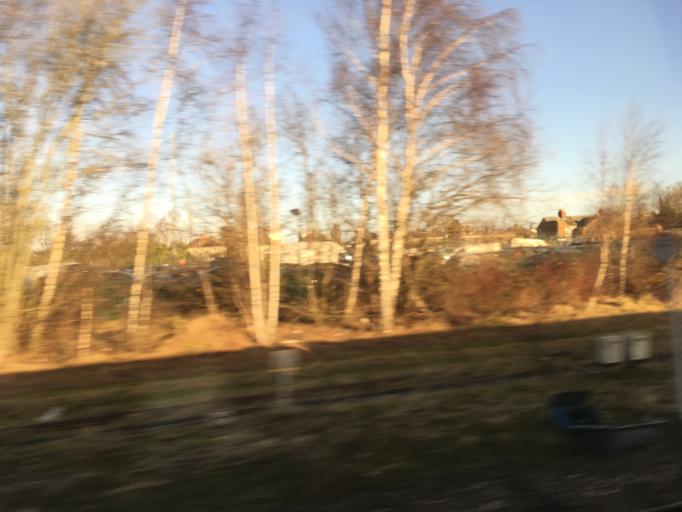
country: GB
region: England
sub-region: Borough of Swindon
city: Swindon
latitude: 51.5709
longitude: -1.7673
